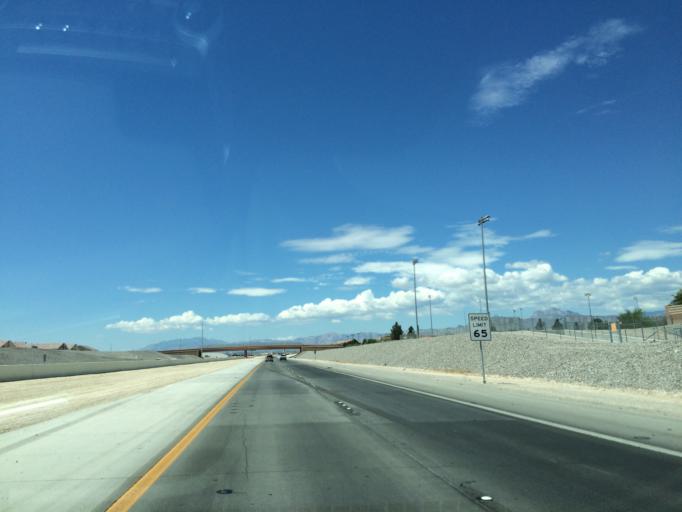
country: US
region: Nevada
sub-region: Clark County
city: North Las Vegas
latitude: 36.2845
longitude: -115.1872
